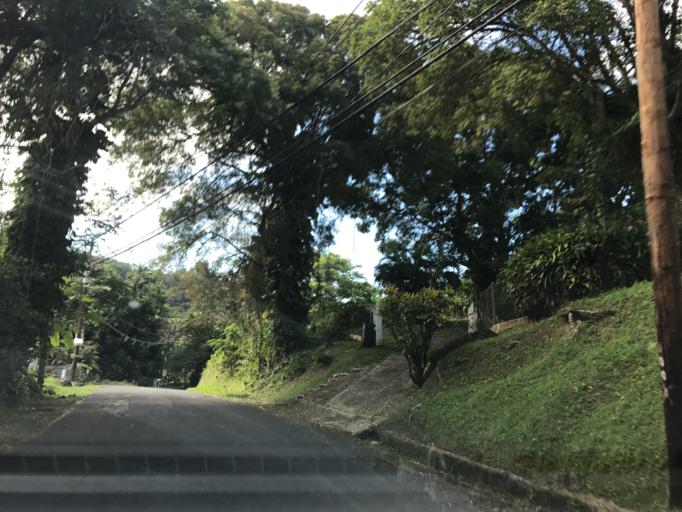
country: PR
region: Luquillo
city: Ramos
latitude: 18.3399
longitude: -65.7297
